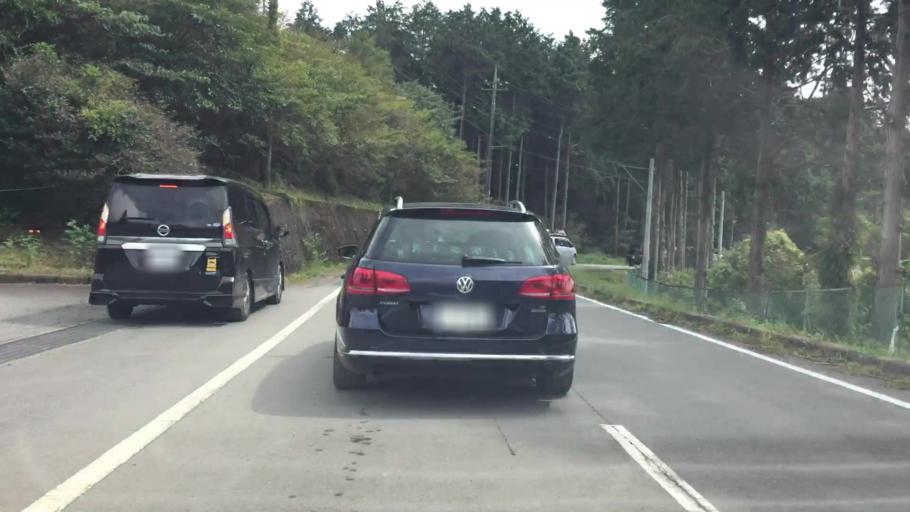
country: JP
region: Yamanashi
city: Fujikawaguchiko
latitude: 35.3935
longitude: 138.5692
